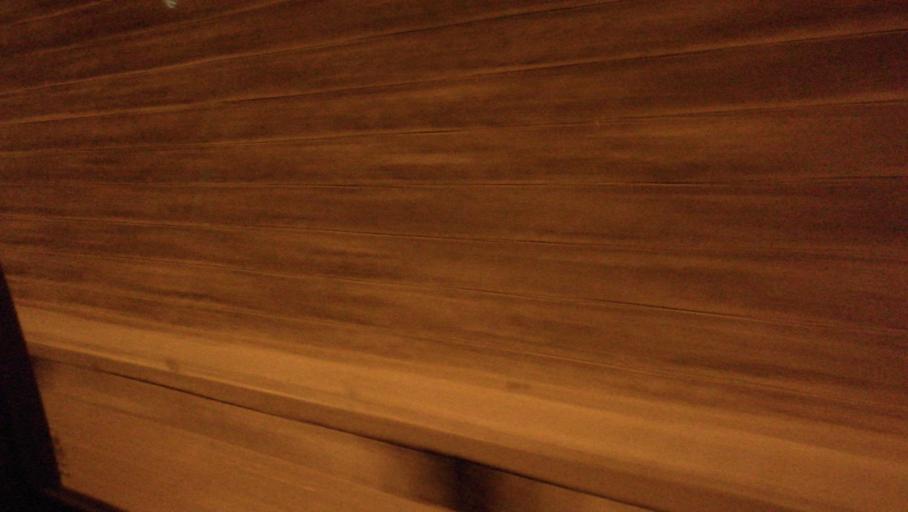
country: IR
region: Alborz
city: Karaj
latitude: 35.8289
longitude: 51.0438
